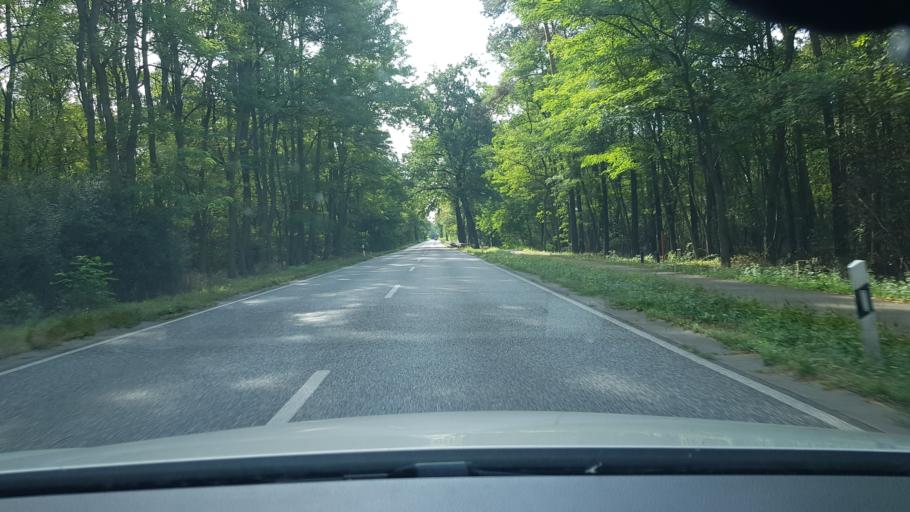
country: DE
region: Brandenburg
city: Lawitz
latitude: 52.1169
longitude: 14.6437
